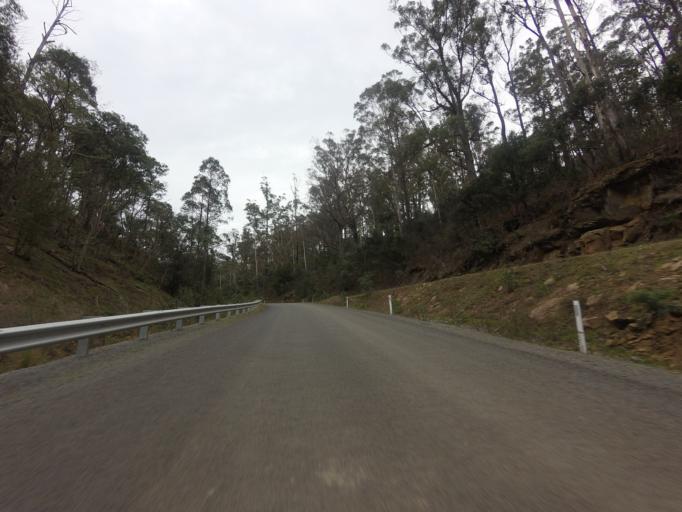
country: AU
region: Tasmania
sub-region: Derwent Valley
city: New Norfolk
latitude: -42.5858
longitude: 147.0120
